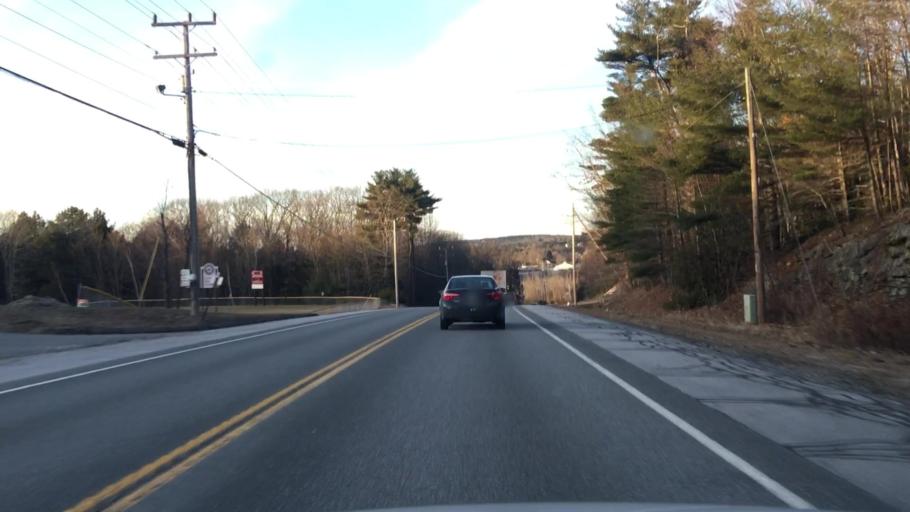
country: US
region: Maine
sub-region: Hancock County
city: Dedham
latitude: 44.7275
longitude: -68.6226
